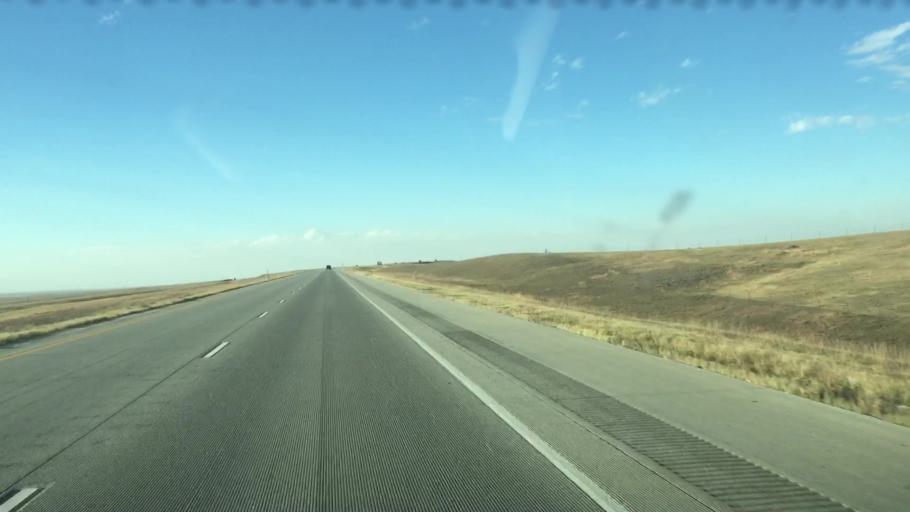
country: US
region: Colorado
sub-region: Lincoln County
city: Limon
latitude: 39.3726
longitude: -103.8825
